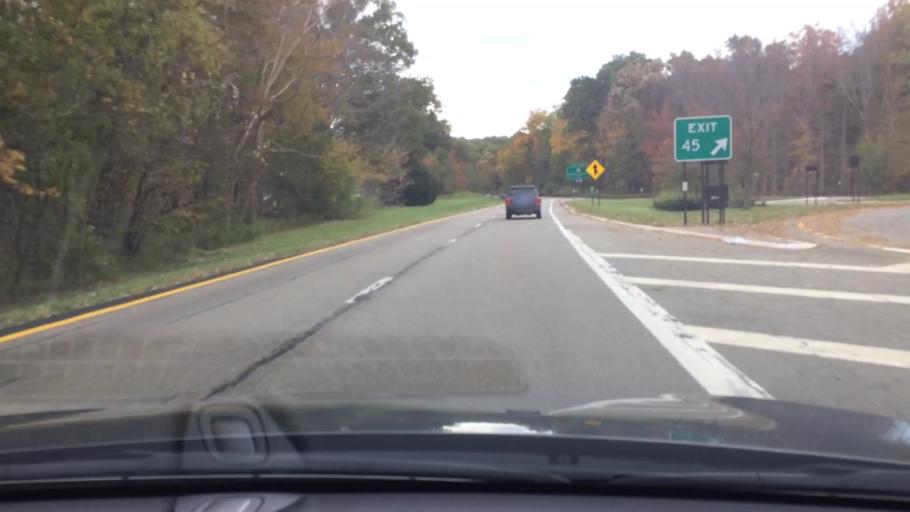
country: US
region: New York
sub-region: Dutchess County
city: Hillside Lake
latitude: 41.6330
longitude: -73.7822
